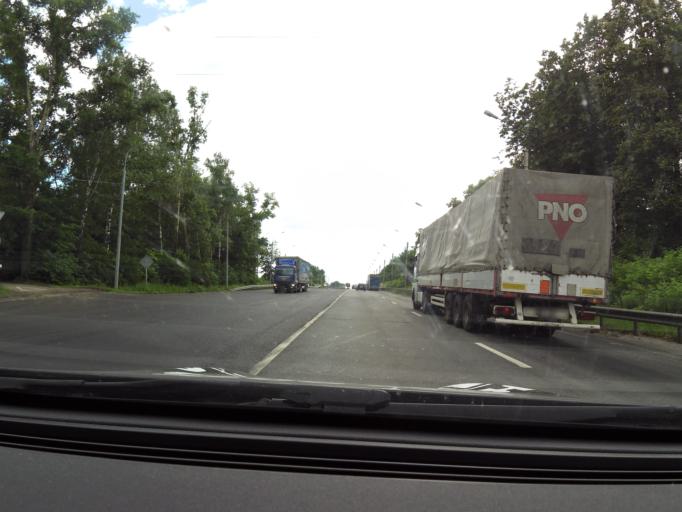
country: RU
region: Vladimir
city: Gorokhovets
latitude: 56.1869
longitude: 42.6762
